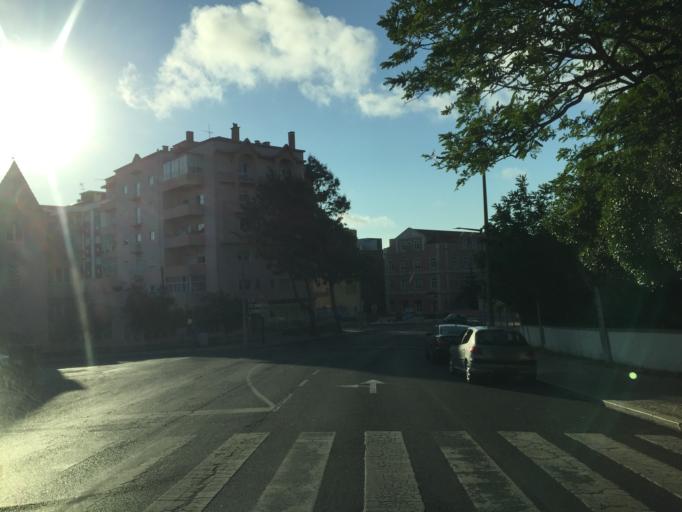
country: PT
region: Leiria
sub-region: Caldas da Rainha
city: Caldas da Rainha
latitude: 39.4002
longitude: -9.1355
